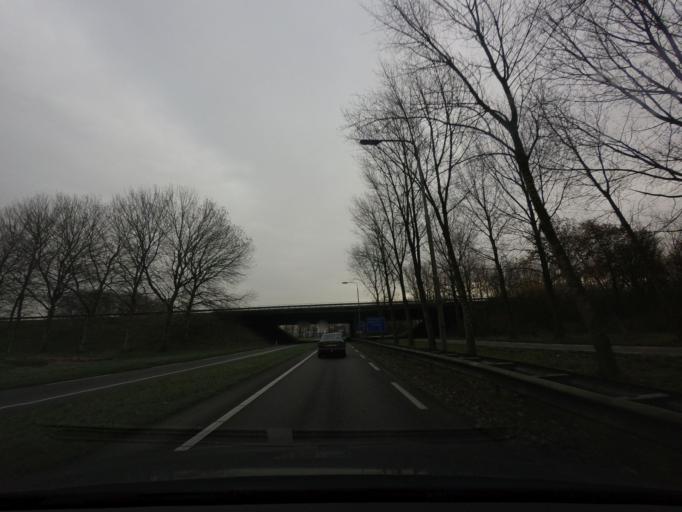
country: NL
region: North Holland
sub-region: Gemeente Medemblik
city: Opperdoes
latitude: 52.8050
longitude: 5.0086
